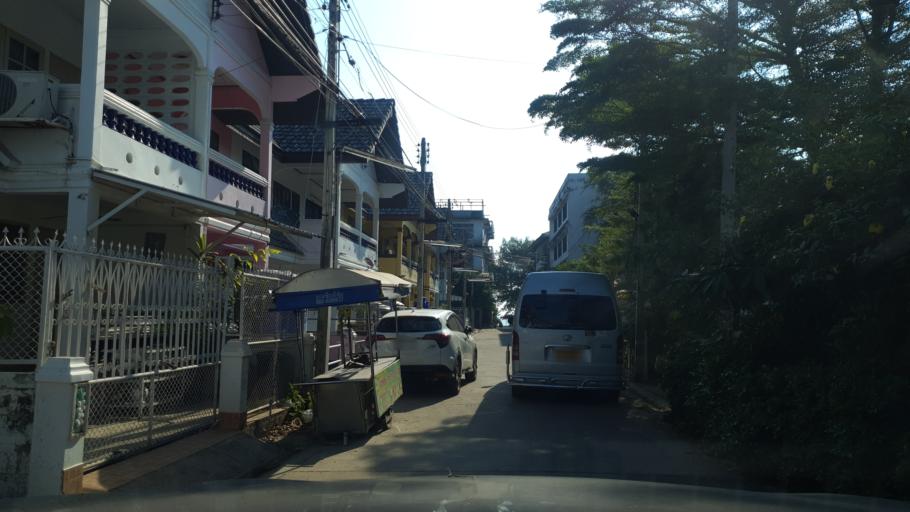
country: TH
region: Phetchaburi
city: Cha-am
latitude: 12.7975
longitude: 99.9839
